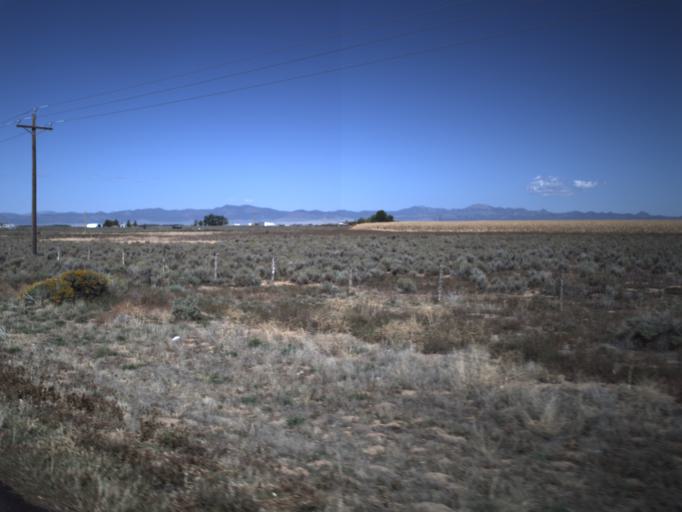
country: US
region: Utah
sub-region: Washington County
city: Enterprise
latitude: 37.6872
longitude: -113.5942
